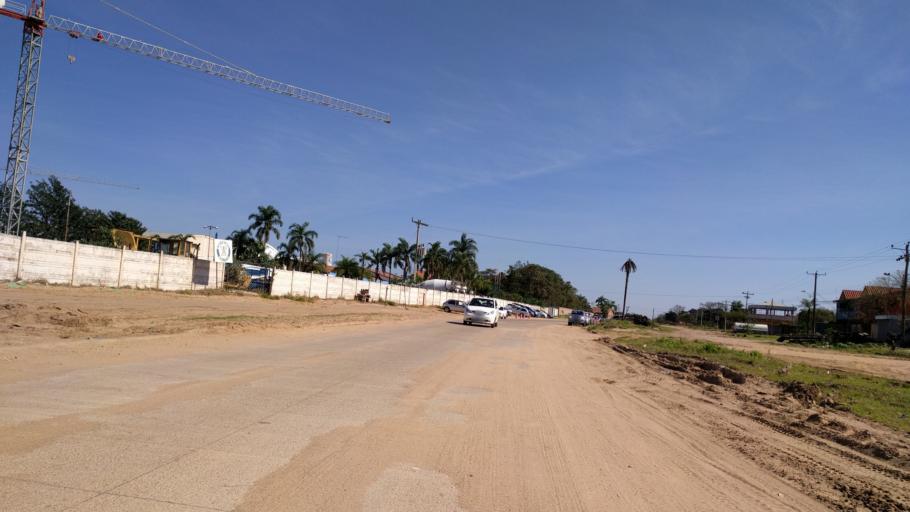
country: BO
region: Santa Cruz
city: Santa Cruz de la Sierra
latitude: -17.8440
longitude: -63.2299
